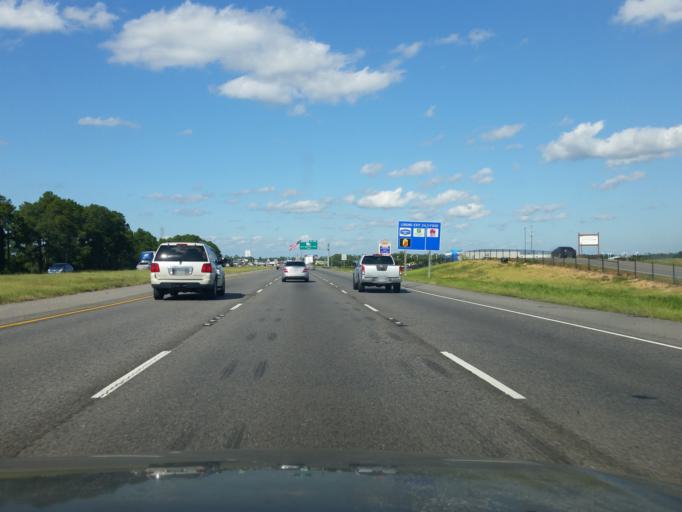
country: US
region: Louisiana
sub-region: Saint Tammany Parish
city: Eden Isle
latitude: 30.2301
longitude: -89.7745
